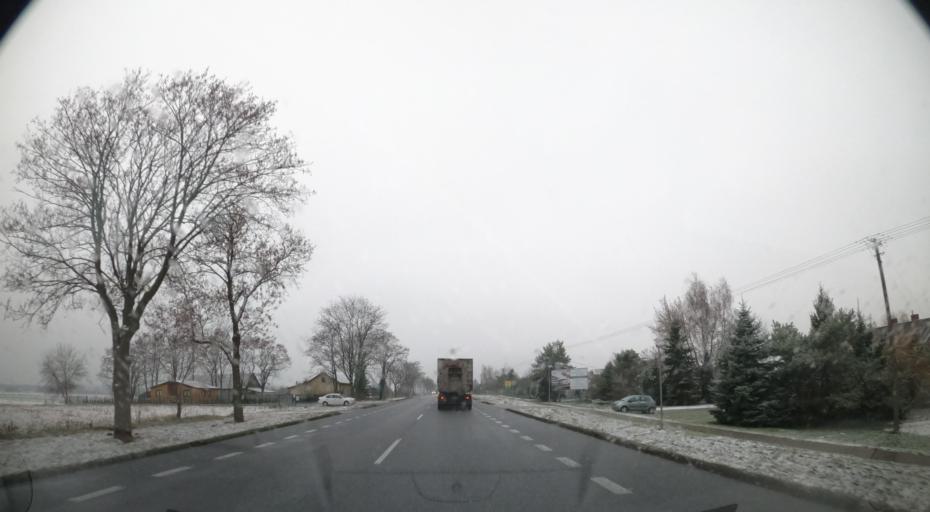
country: PL
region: Masovian Voivodeship
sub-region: Powiat sochaczewski
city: Teresin
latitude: 52.2183
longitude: 20.3608
